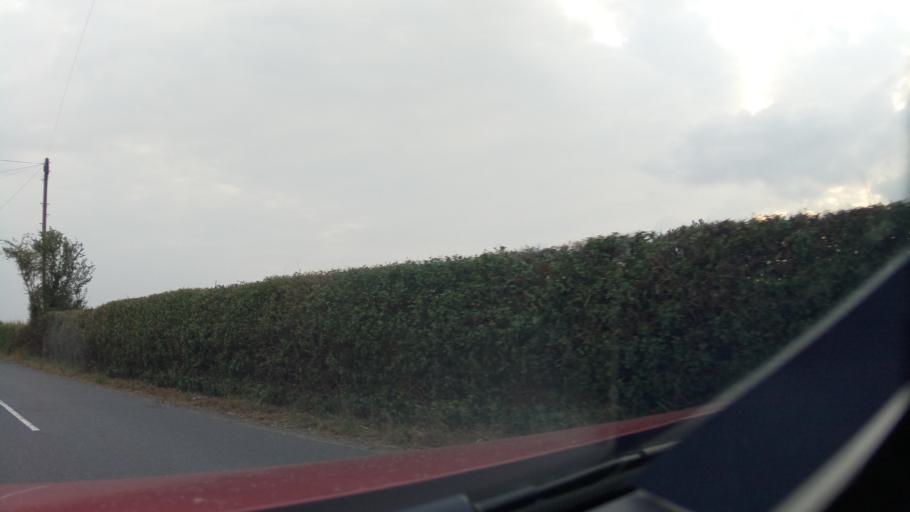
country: GB
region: England
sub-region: Lincolnshire
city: Skellingthorpe
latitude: 53.1404
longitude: -0.6459
